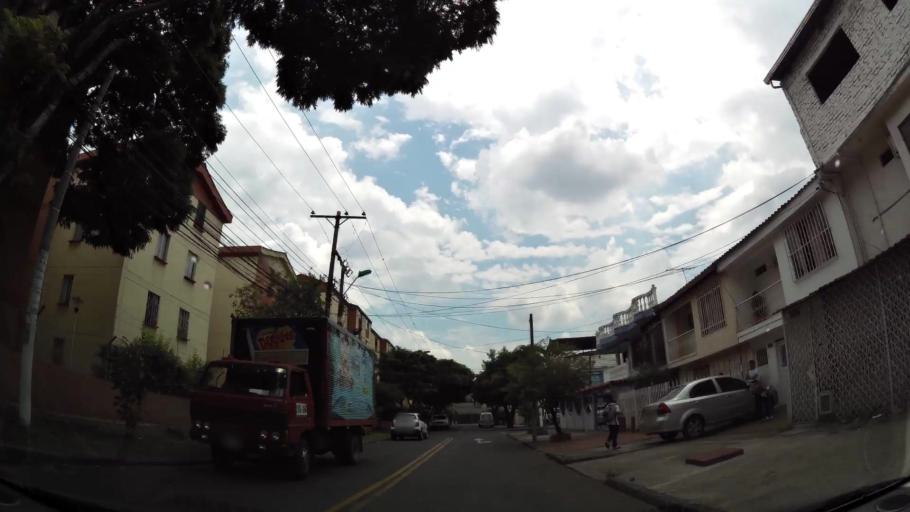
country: CO
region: Valle del Cauca
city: Cali
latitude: 3.4647
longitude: -76.4992
